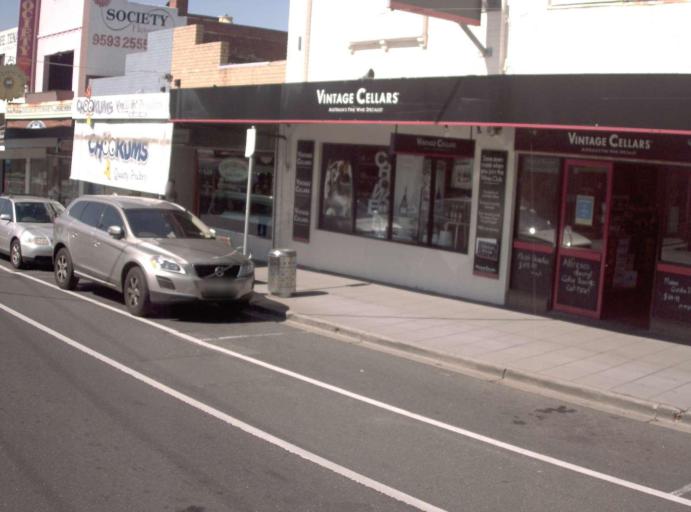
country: AU
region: Victoria
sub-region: Bayside
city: Hampton
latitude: -37.9286
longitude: 145.0041
